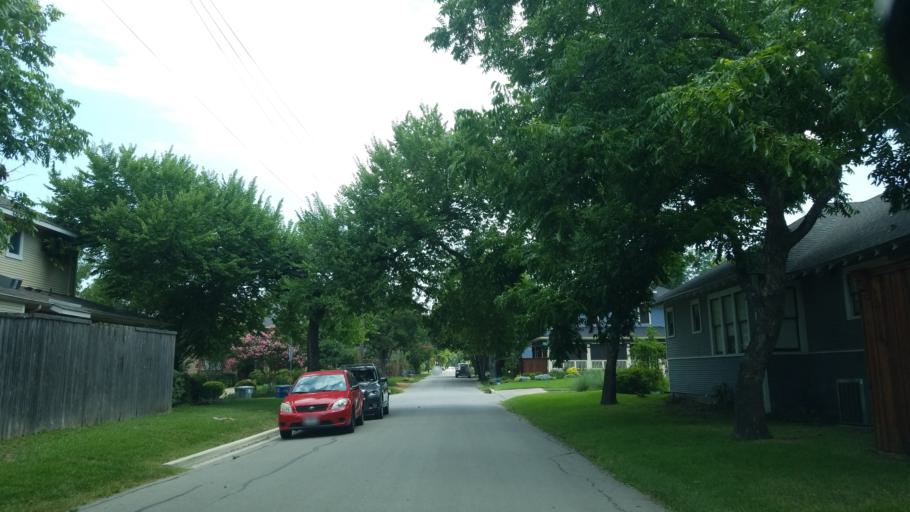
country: US
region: Texas
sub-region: Dallas County
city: Highland Park
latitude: 32.8209
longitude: -96.7723
